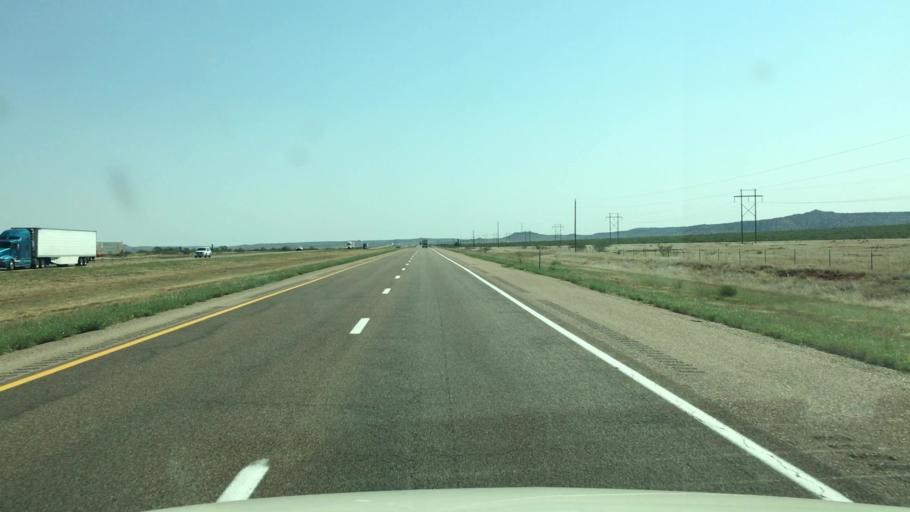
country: US
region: New Mexico
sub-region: Quay County
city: Tucumcari
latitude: 35.1089
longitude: -104.0144
